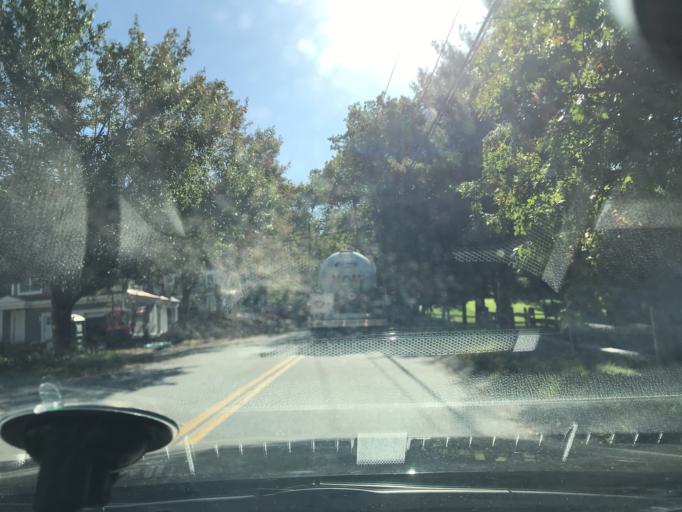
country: US
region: Massachusetts
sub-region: Norfolk County
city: Wellesley
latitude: 42.2860
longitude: -71.2932
